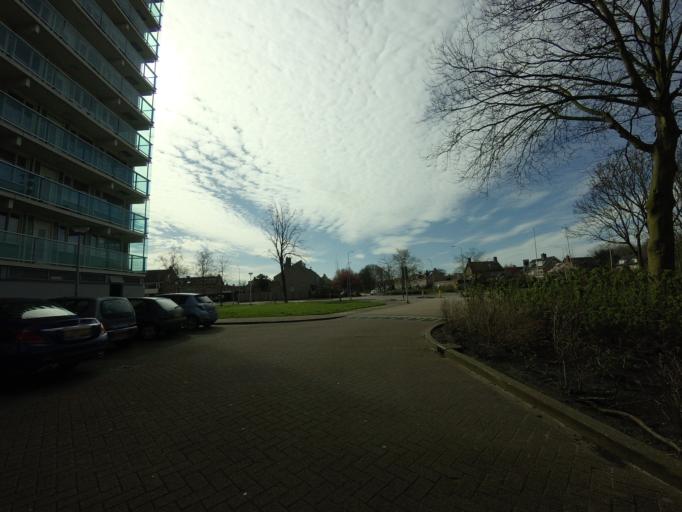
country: NL
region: North Holland
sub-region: Gemeente Uithoorn
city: Uithoorn
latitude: 52.2469
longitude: 4.8356
